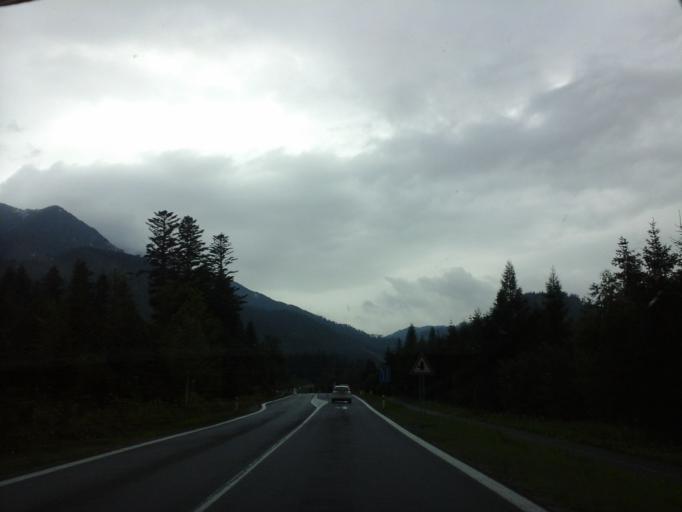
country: SK
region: Presovsky
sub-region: Okres Poprad
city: Zdiar
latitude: 49.2194
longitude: 20.3346
